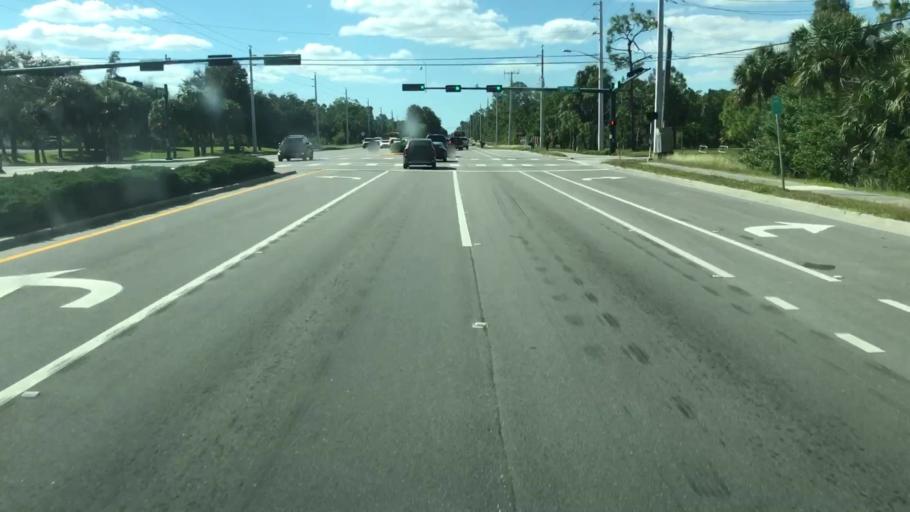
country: US
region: Florida
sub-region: Collier County
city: Golden Gate
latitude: 26.2296
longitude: -81.6324
